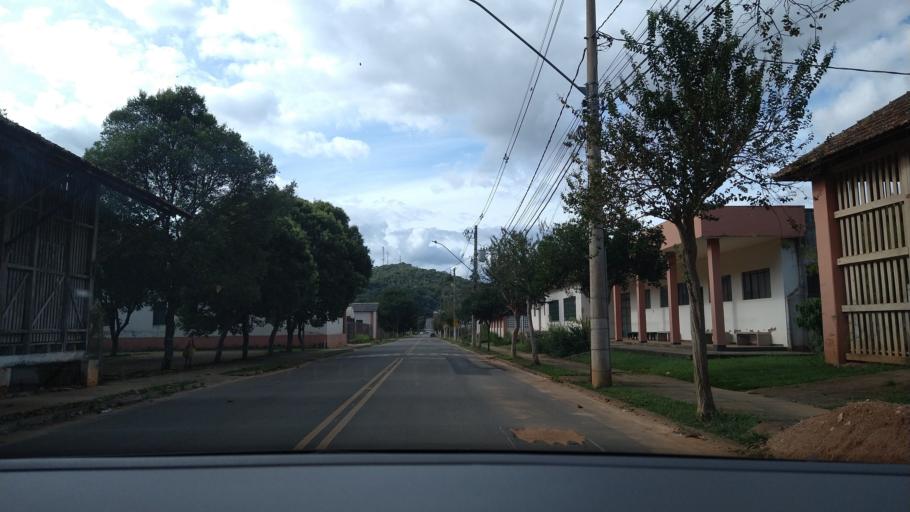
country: BR
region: Minas Gerais
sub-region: Vicosa
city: Vicosa
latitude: -20.7684
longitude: -42.8708
